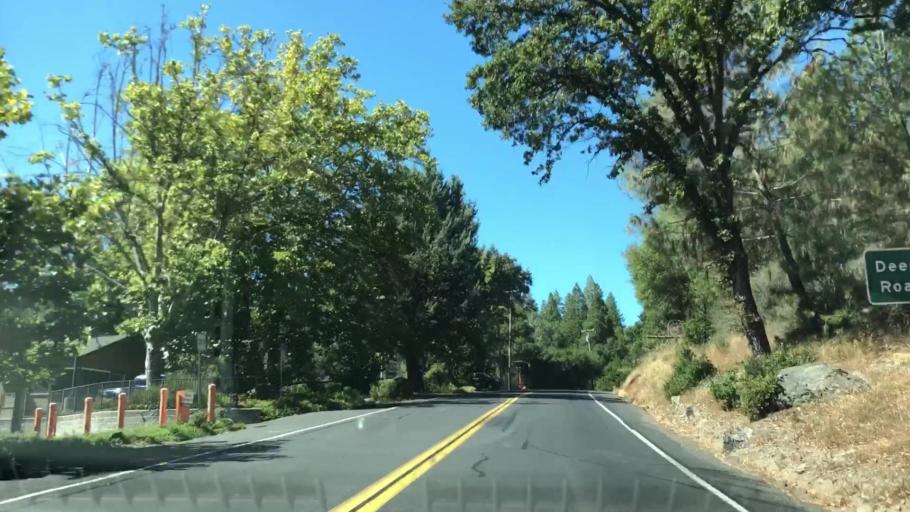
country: US
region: California
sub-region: Tuolumne County
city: Tuolumne City
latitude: 37.8370
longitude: -120.2348
